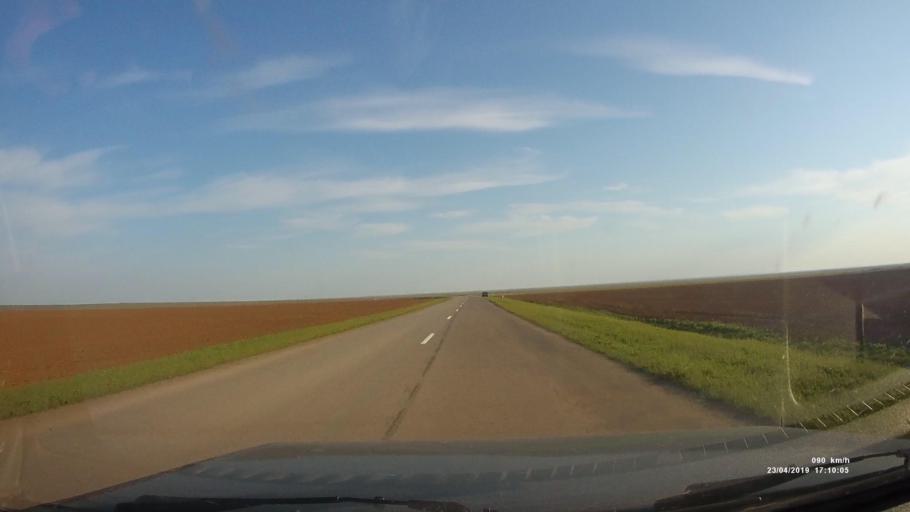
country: RU
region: Kalmykiya
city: Priyutnoye
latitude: 46.2493
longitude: 43.4841
